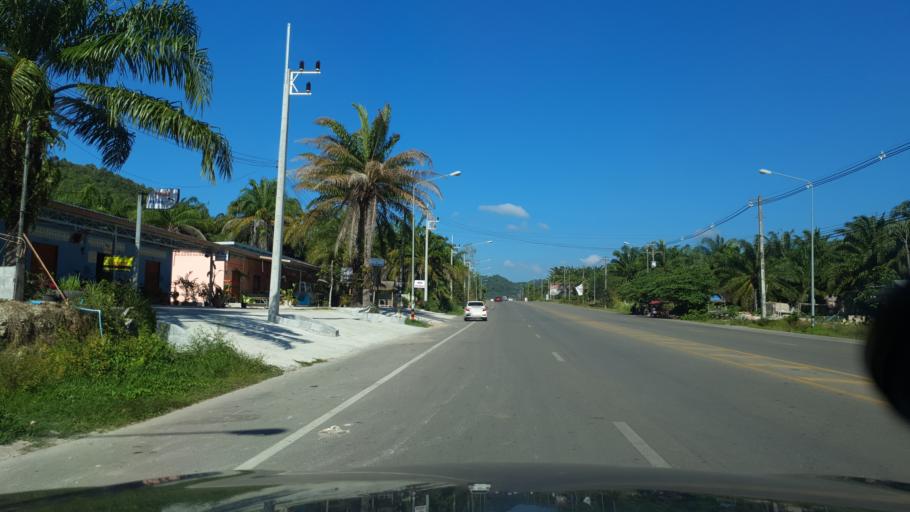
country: TH
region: Phangnga
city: Ban Ao Nang
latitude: 8.0361
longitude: 98.8561
